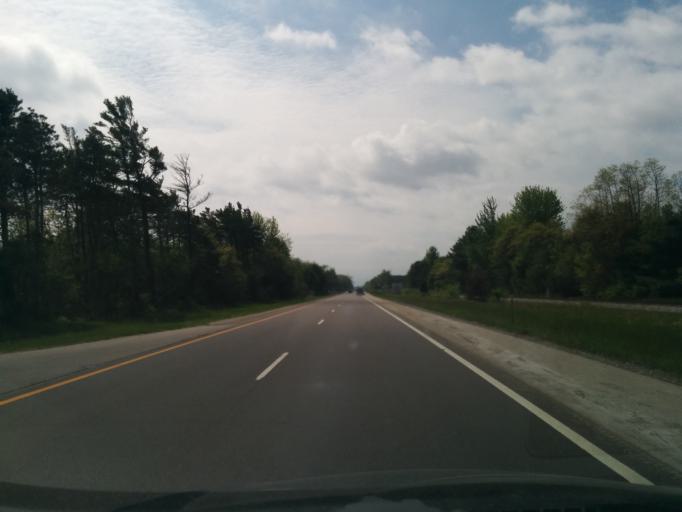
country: US
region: Michigan
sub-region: Ottawa County
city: Grand Haven
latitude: 43.0052
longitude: -86.2038
